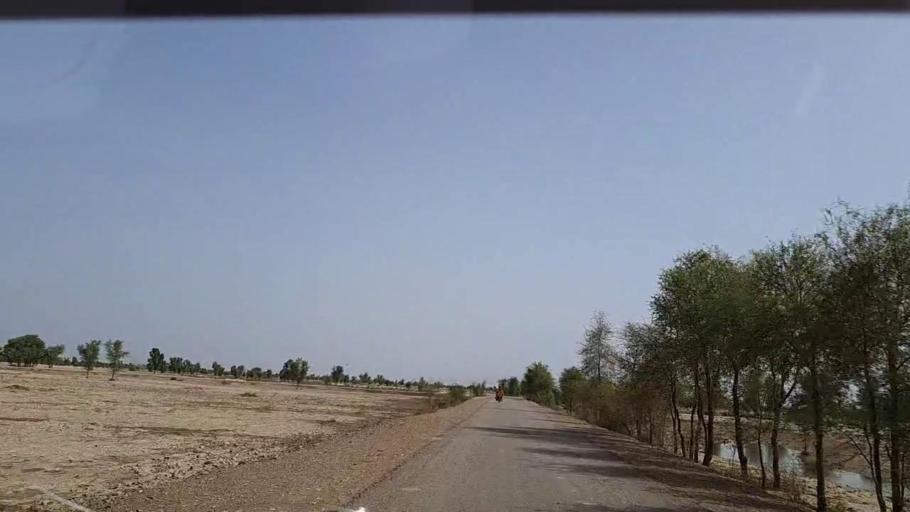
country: PK
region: Sindh
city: Johi
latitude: 26.6255
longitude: 67.5007
